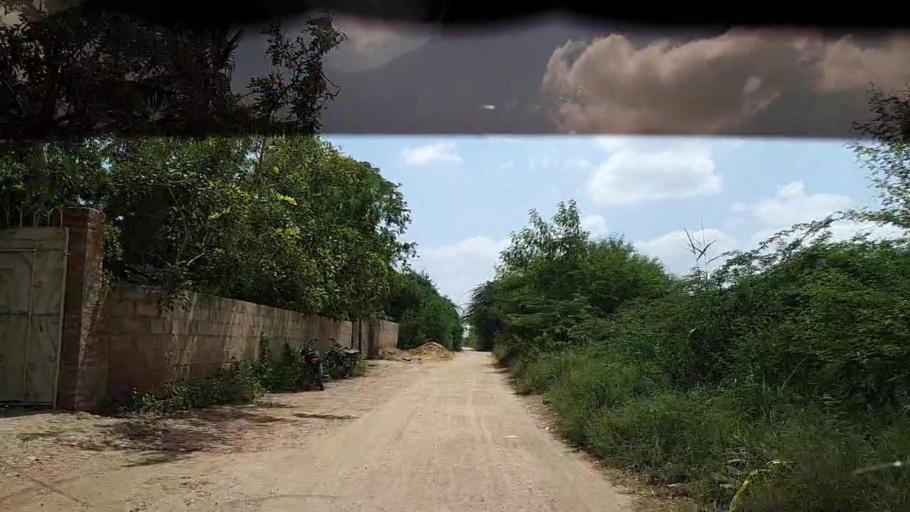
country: PK
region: Sindh
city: Kadhan
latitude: 24.5883
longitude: 68.9583
